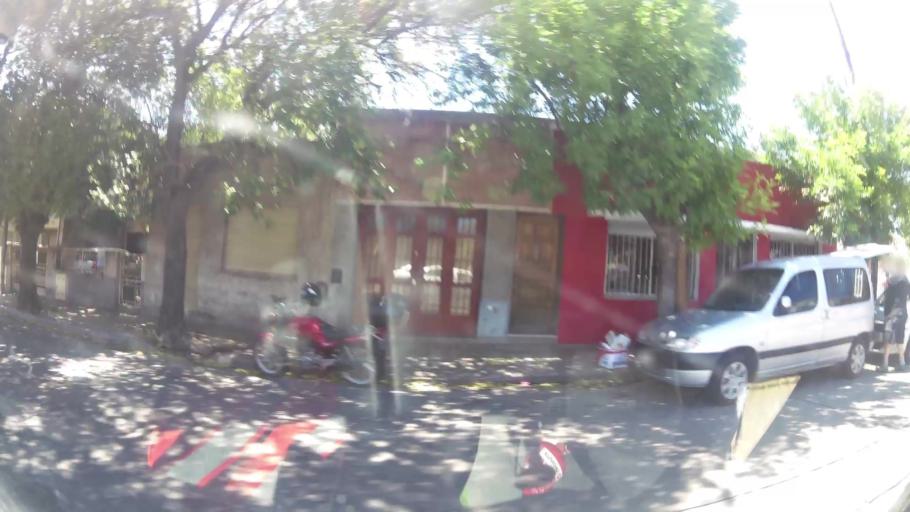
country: AR
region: Cordoba
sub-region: Departamento de Capital
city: Cordoba
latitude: -31.4144
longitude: -64.2260
